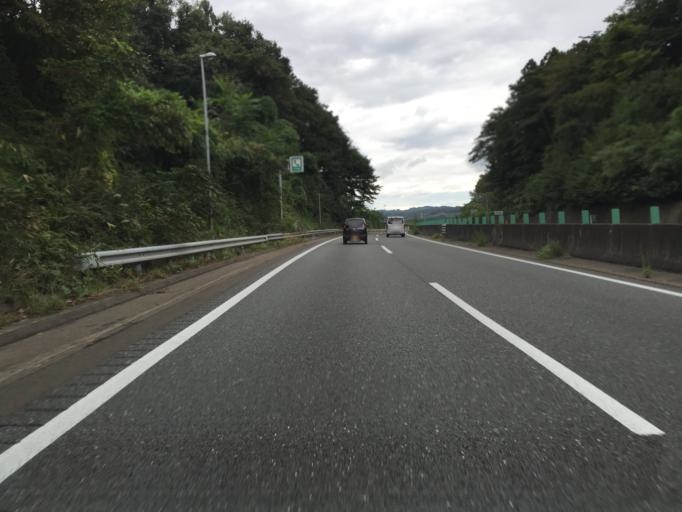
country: JP
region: Miyagi
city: Okawara
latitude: 38.1023
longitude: 140.6886
